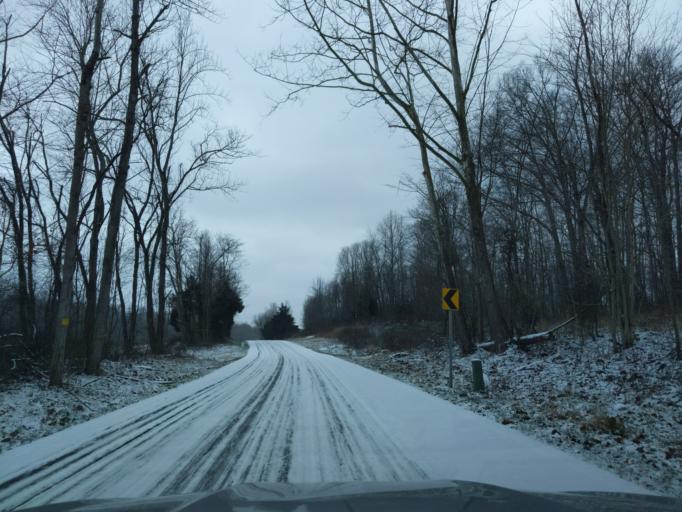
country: US
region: Indiana
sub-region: Decatur County
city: Westport
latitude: 39.2115
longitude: -85.5205
